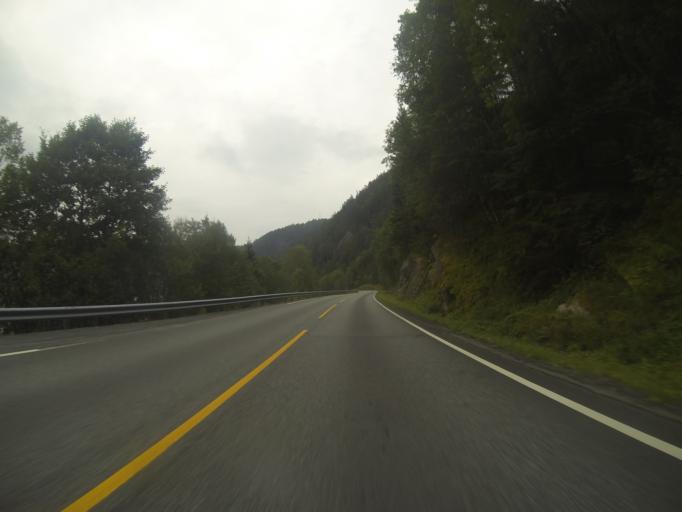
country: NO
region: Rogaland
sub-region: Suldal
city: Sand
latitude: 59.4740
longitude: 6.1947
